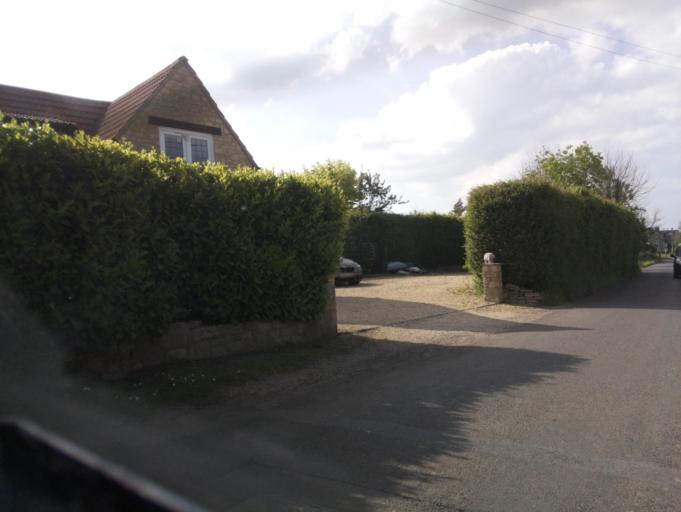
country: GB
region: England
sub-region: Wiltshire
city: Bremhill
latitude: 51.5058
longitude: -2.0743
